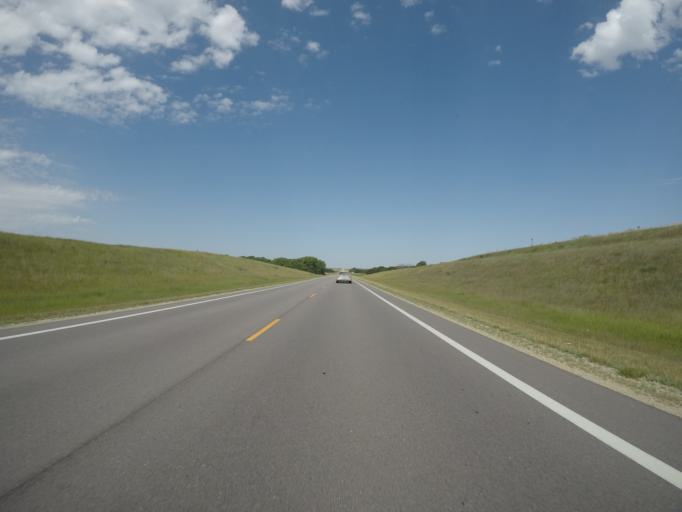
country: US
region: Kansas
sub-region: Clay County
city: Clay Center
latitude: 39.3789
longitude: -97.3006
